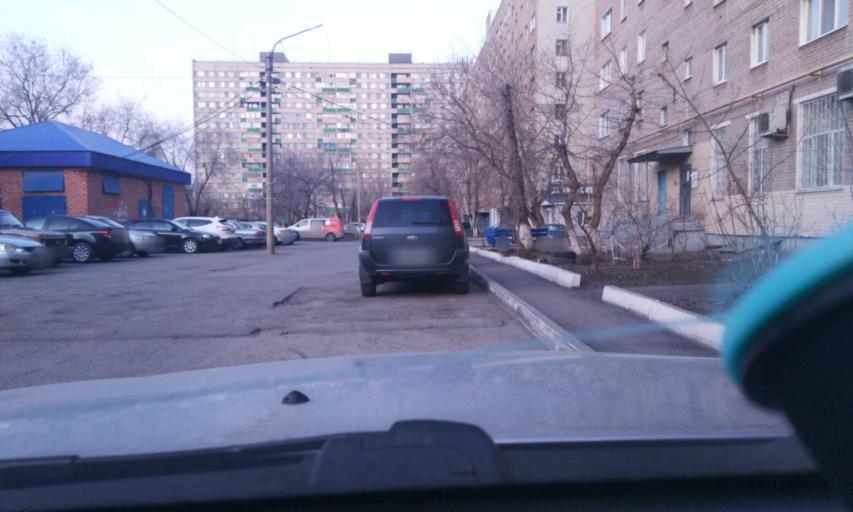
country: RU
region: Orenburg
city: Orenburg
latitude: 51.7650
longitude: 55.1171
